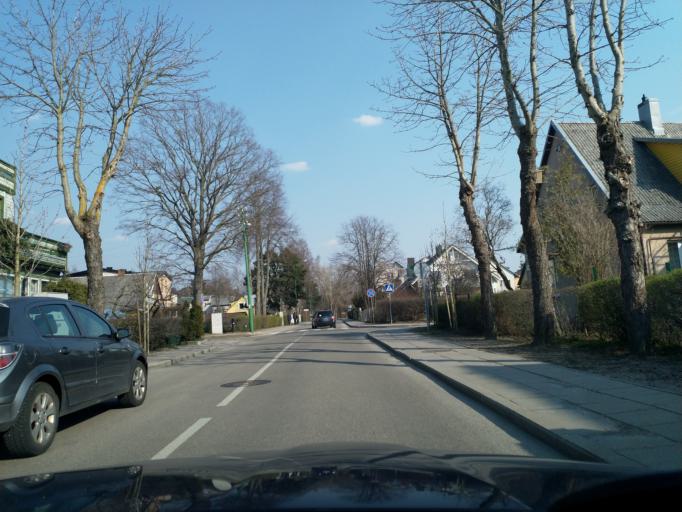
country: LT
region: Klaipedos apskritis
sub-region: Klaipeda
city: Palanga
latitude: 55.9118
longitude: 21.0705
